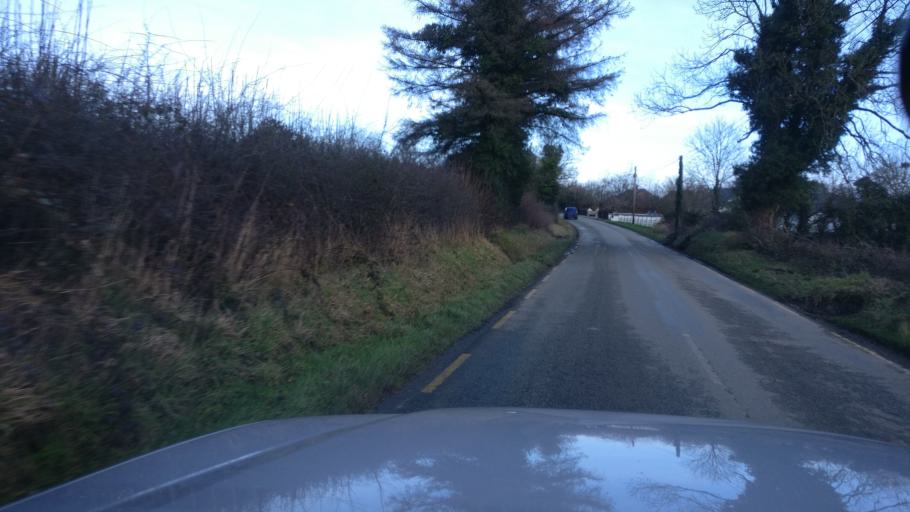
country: IE
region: Leinster
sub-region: Kilkenny
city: Castlecomer
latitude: 52.8328
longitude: -7.1966
